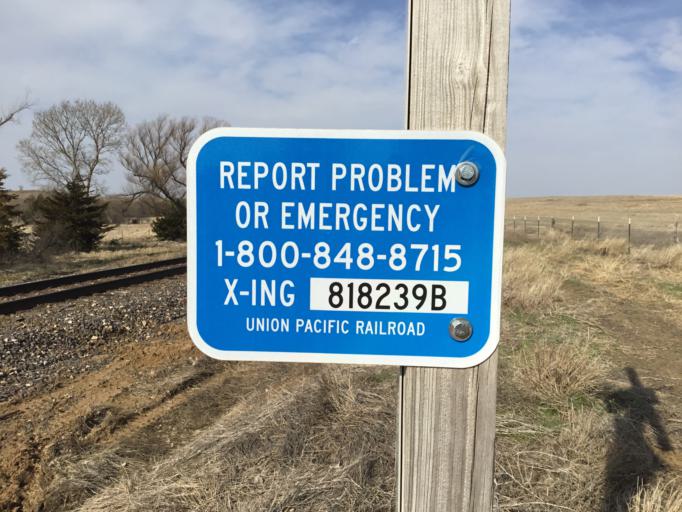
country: US
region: Kansas
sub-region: Ellsworth County
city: Ellsworth
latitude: 38.7356
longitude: -98.0584
